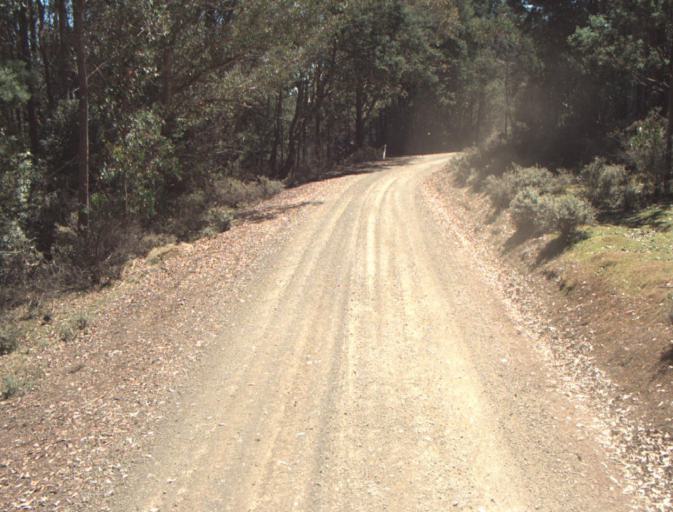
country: AU
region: Tasmania
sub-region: Dorset
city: Scottsdale
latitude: -41.3554
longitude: 147.4254
